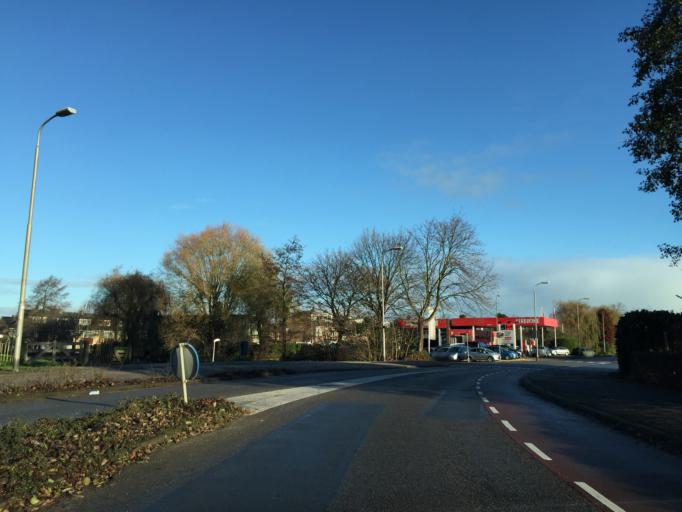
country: NL
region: South Holland
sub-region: Gemeente Den Haag
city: Ypenburg
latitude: 52.0396
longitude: 4.3872
